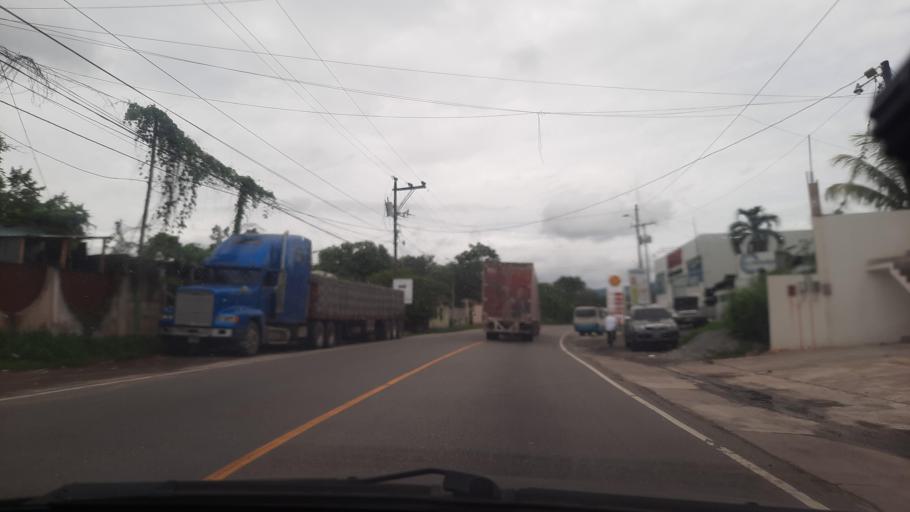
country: GT
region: Izabal
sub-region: Municipio de Los Amates
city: Los Amates
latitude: 15.2594
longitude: -89.0893
